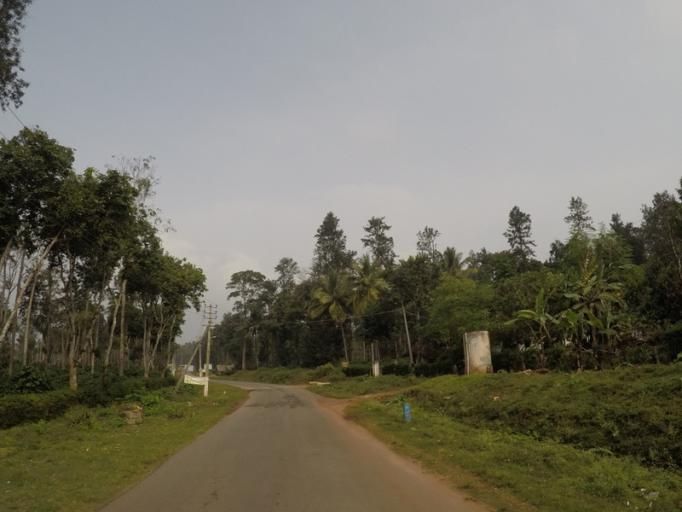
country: IN
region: Karnataka
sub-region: Chikmagalur
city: Koppa
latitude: 13.3515
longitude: 75.4748
